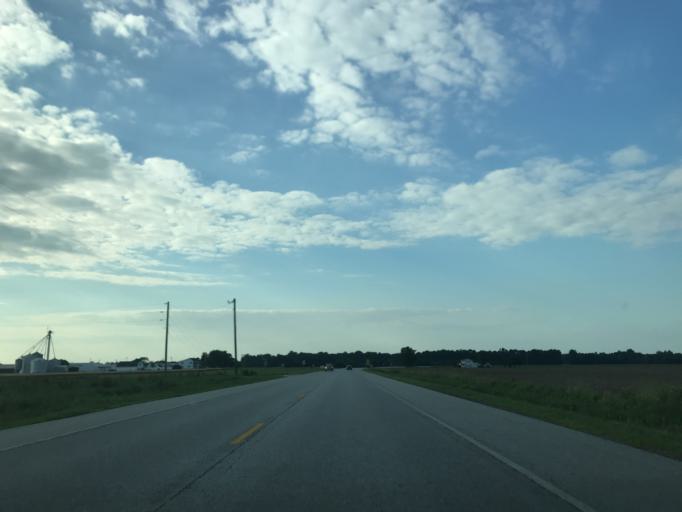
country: US
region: Maryland
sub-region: Caroline County
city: Federalsburg
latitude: 38.7431
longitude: -75.7934
